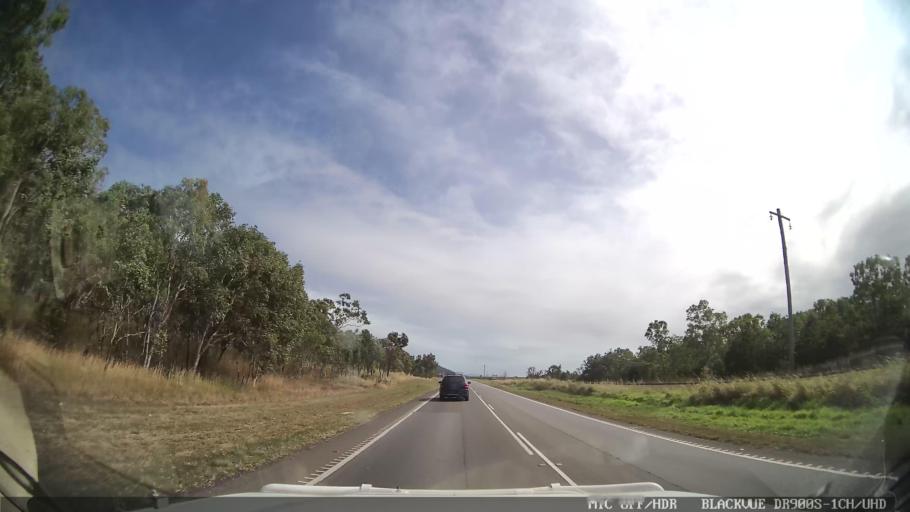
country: AU
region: Queensland
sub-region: Townsville
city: Townsville
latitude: -19.4004
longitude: 147.0246
